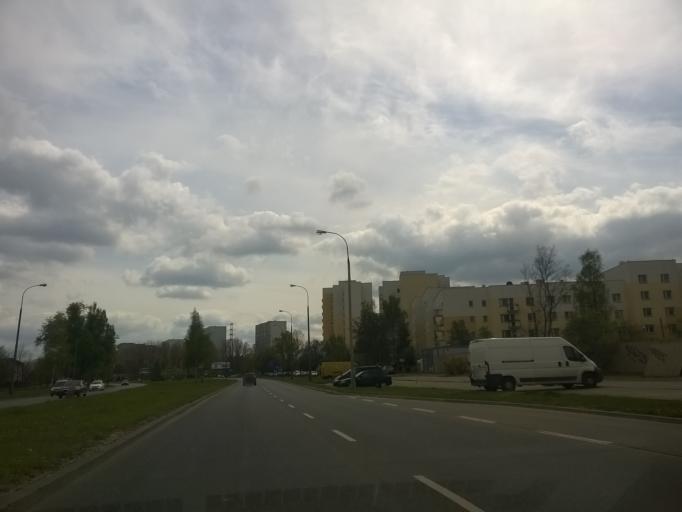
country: PL
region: Masovian Voivodeship
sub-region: Warszawa
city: Ursynow
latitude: 52.1582
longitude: 21.0420
